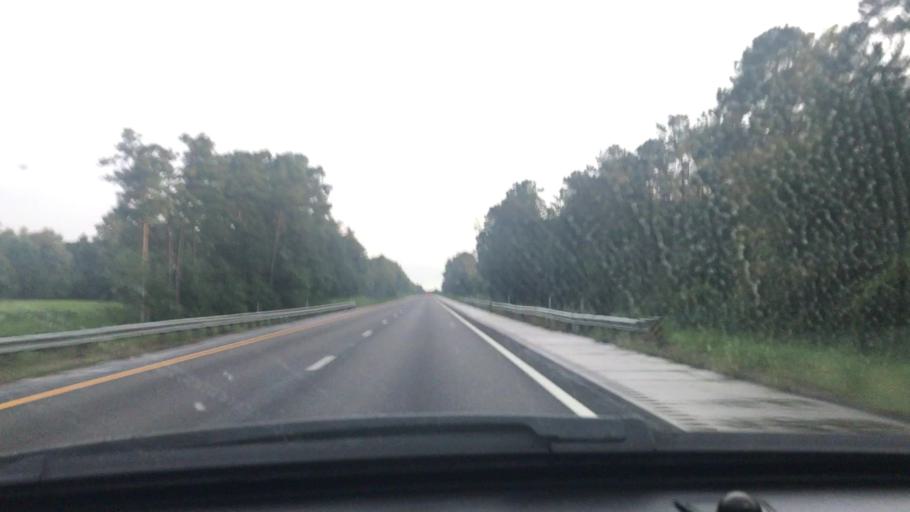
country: US
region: Mississippi
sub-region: Pike County
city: Magnolia
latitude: 31.0759
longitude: -90.4915
